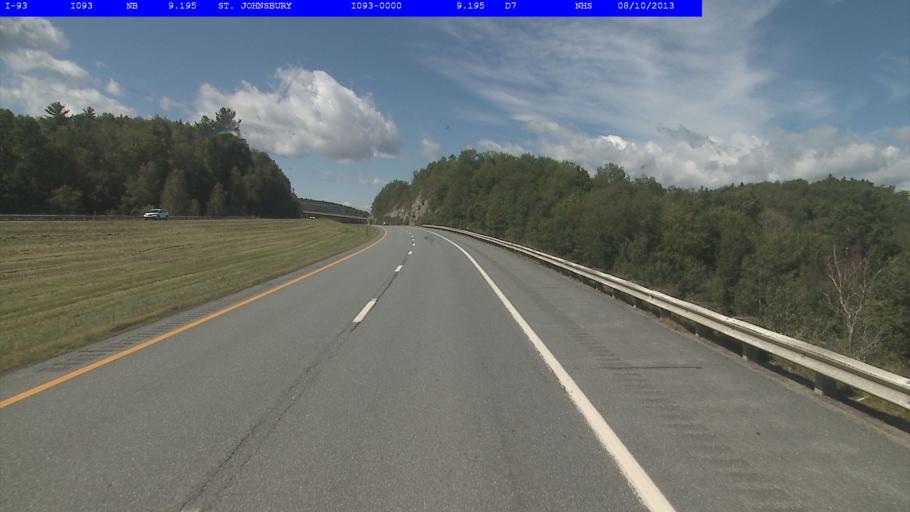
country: US
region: Vermont
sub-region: Caledonia County
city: Saint Johnsbury
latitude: 44.4148
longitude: -71.9848
